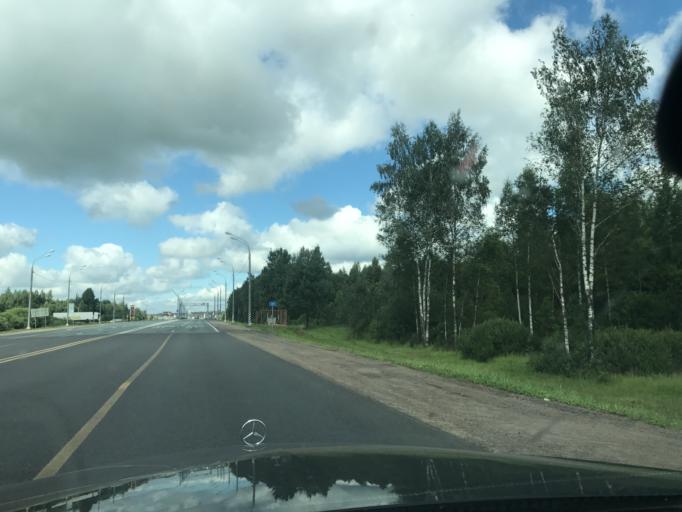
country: RU
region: Smolensk
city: Rudnya
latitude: 54.6903
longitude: 31.0406
